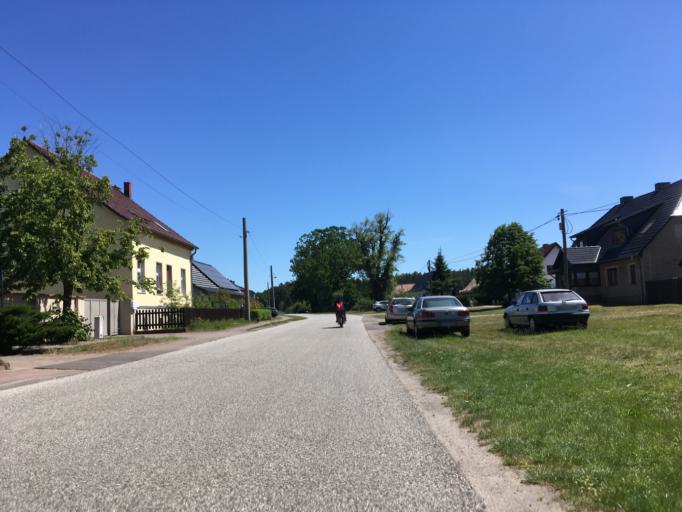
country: DE
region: Brandenburg
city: Zehdenick
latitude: 52.9821
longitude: 13.3825
